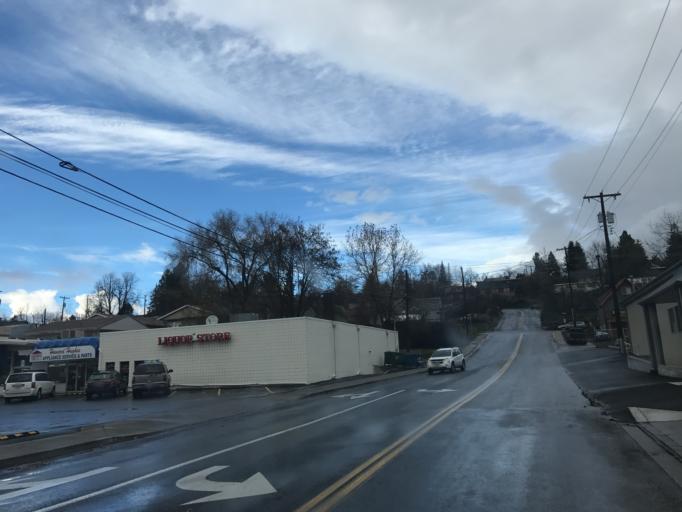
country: US
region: Idaho
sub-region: Latah County
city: Moscow
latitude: 46.7336
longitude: -117.0120
